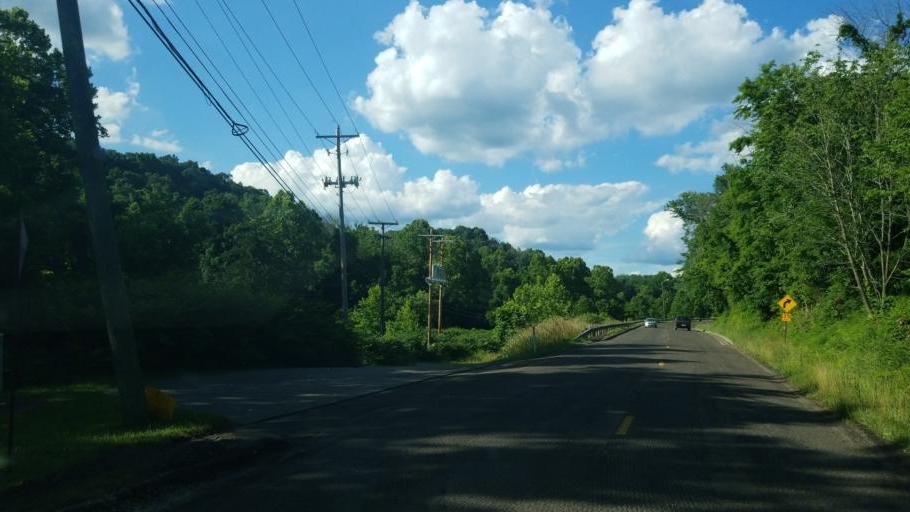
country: US
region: Ohio
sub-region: Gallia County
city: Gallipolis
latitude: 38.8045
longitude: -82.2221
